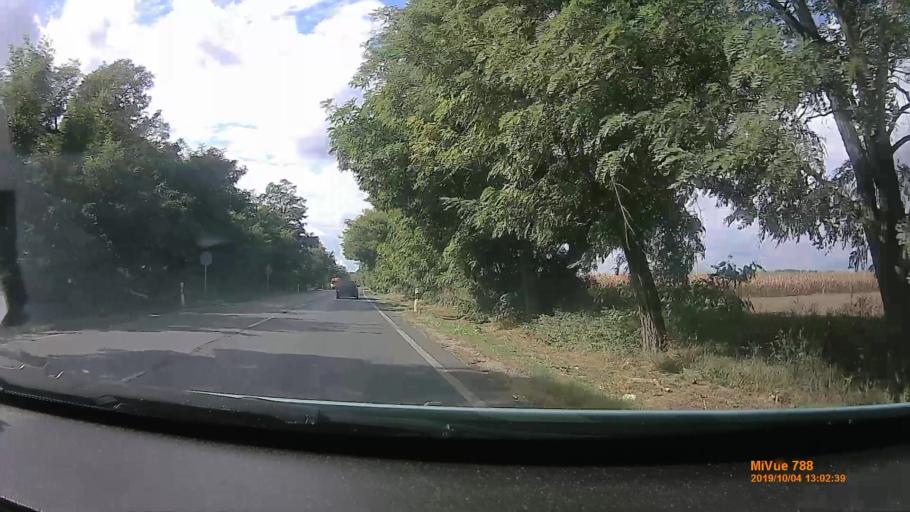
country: HU
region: Szabolcs-Szatmar-Bereg
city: Nyirtelek
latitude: 47.9572
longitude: 21.6488
